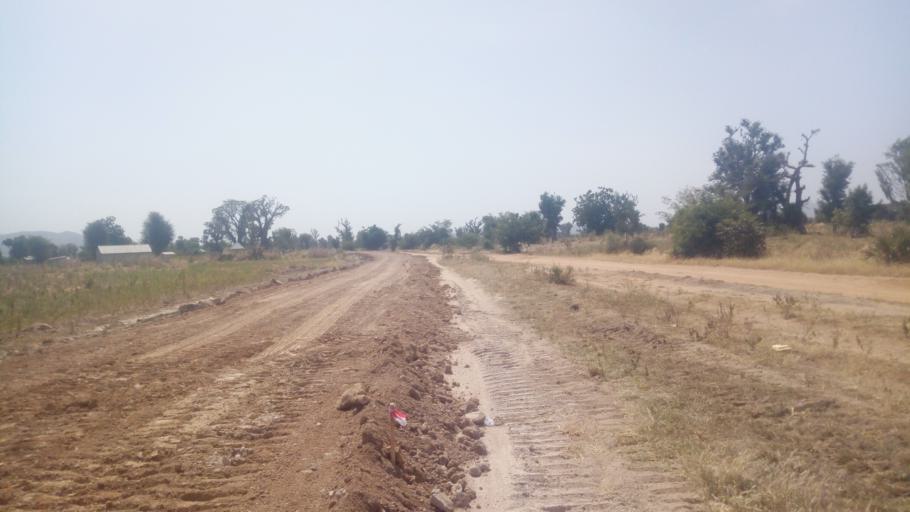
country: NG
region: Adamawa
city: Yola
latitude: 9.1795
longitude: 12.4035
